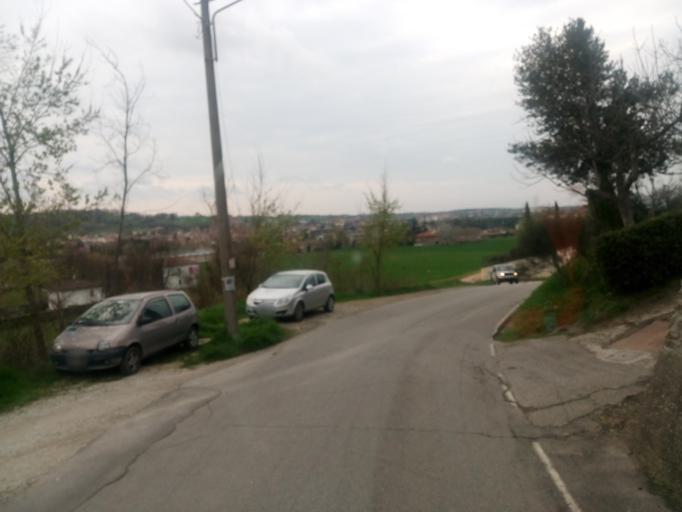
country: IT
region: Emilia-Romagna
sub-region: Forli-Cesena
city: Meldola
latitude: 44.1185
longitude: 12.0684
